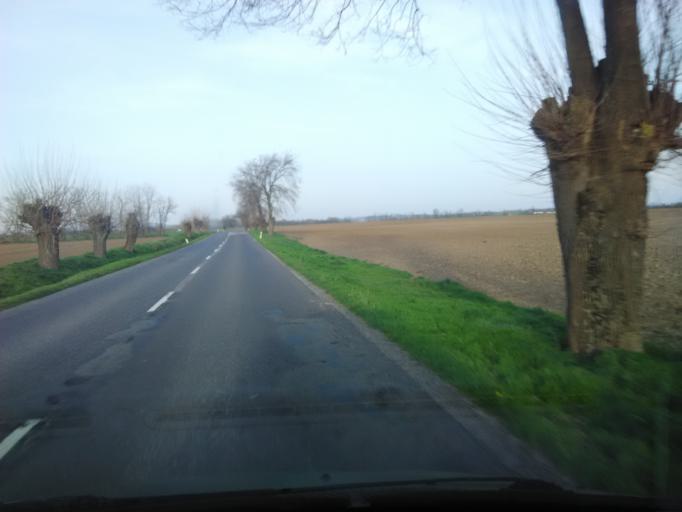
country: SK
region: Nitriansky
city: Tlmace
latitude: 48.1877
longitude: 18.4888
